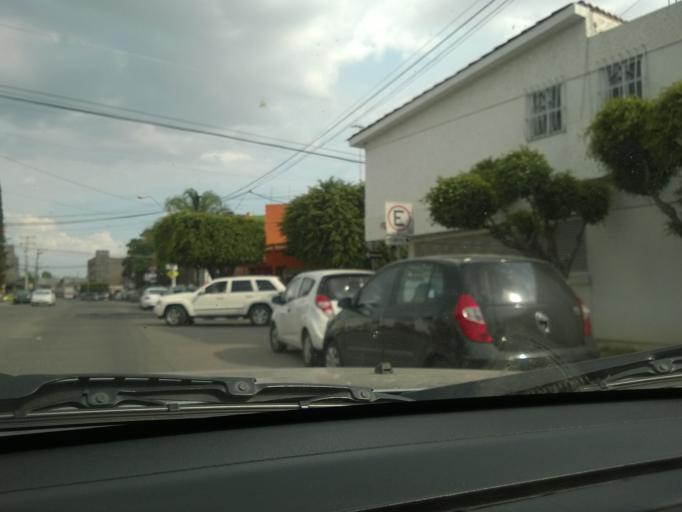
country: MX
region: Guanajuato
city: Leon
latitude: 21.1506
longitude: -101.6889
